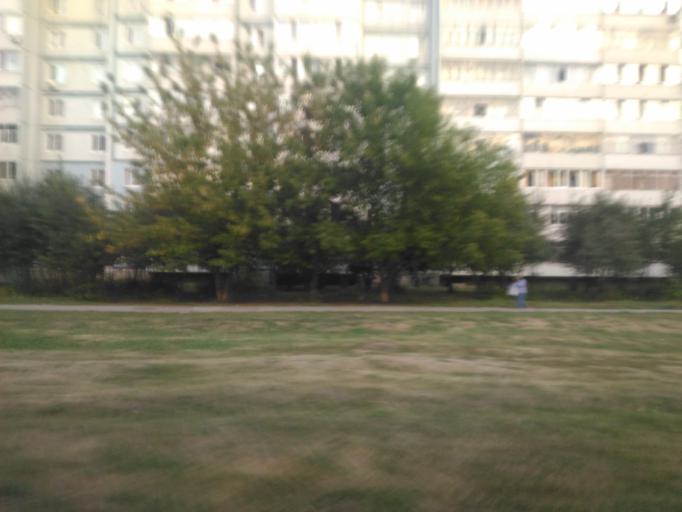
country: RU
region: Ulyanovsk
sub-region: Ulyanovskiy Rayon
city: Ulyanovsk
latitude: 54.2685
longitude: 48.2846
